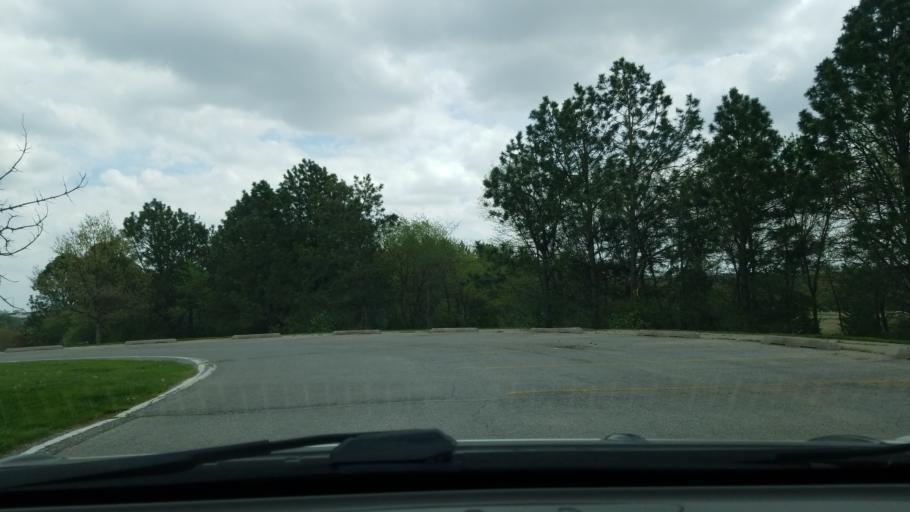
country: US
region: Nebraska
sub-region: Sarpy County
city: Chalco
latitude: 41.1653
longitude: -96.1601
